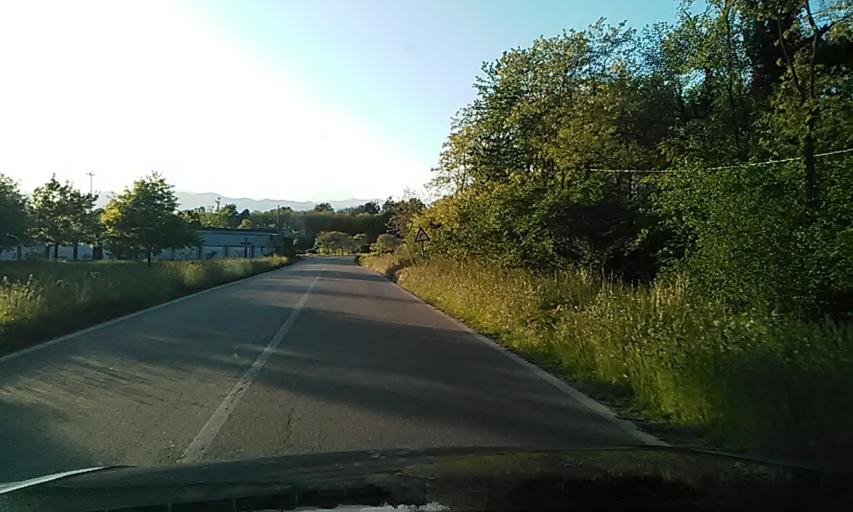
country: IT
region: Piedmont
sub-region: Provincia di Vercelli
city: Rovasenda
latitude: 45.5301
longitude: 8.3167
